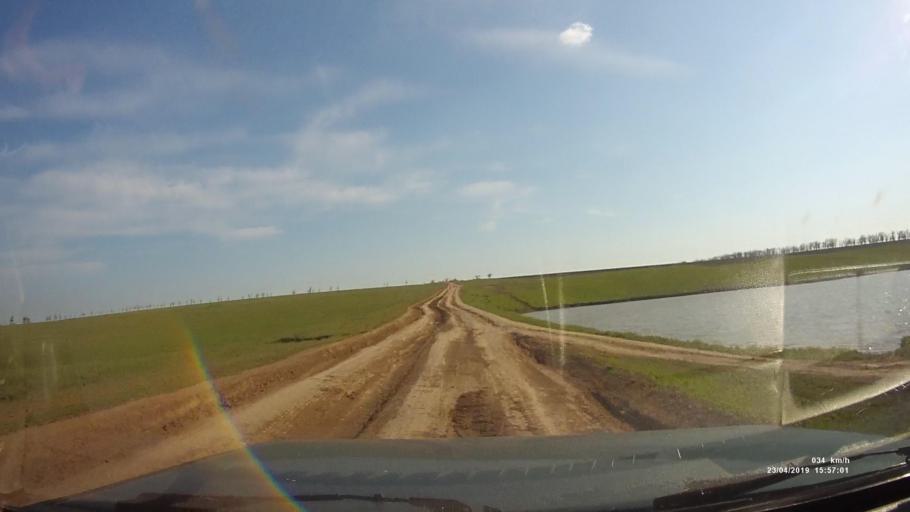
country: RU
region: Rostov
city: Remontnoye
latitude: 46.5342
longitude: 43.1105
